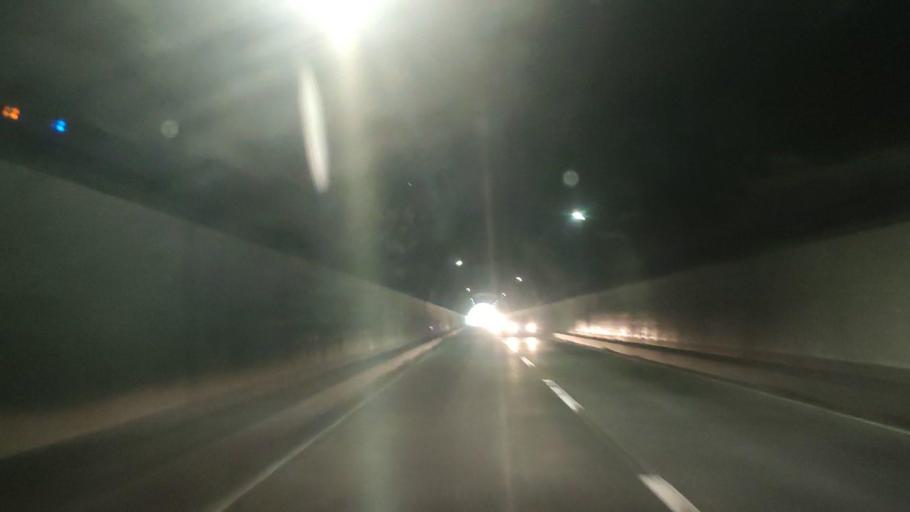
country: JP
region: Kagoshima
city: Okuchi-shinohara
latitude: 31.9736
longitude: 130.7410
